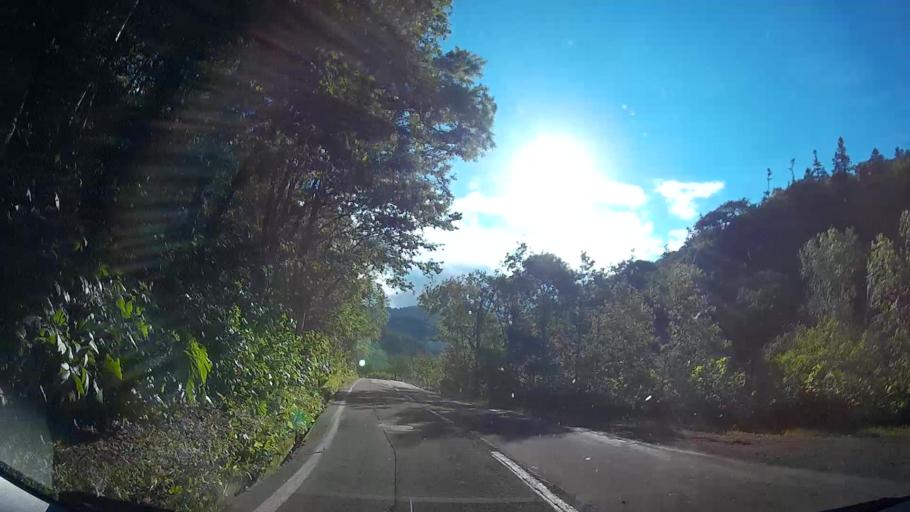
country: JP
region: Hokkaido
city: Otaru
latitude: 42.9826
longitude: 141.0496
